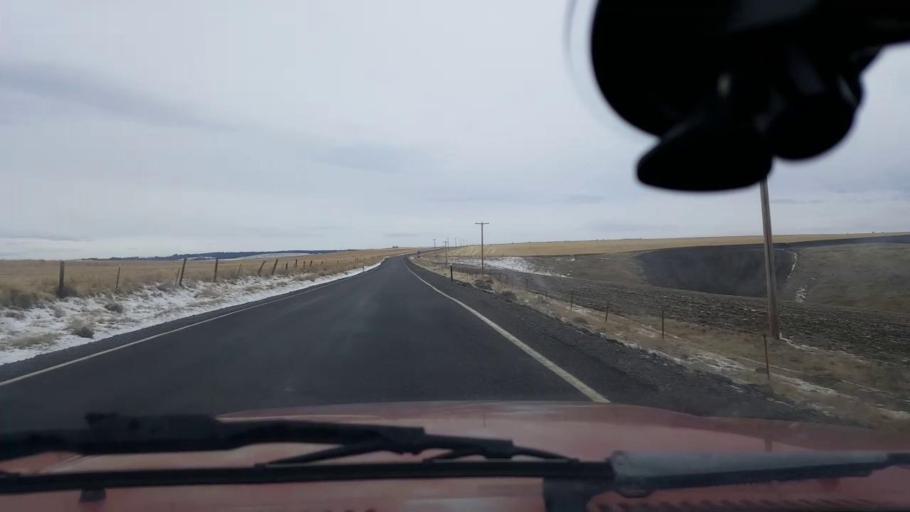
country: US
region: Washington
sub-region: Garfield County
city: Pomeroy
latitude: 46.3237
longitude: -117.3675
